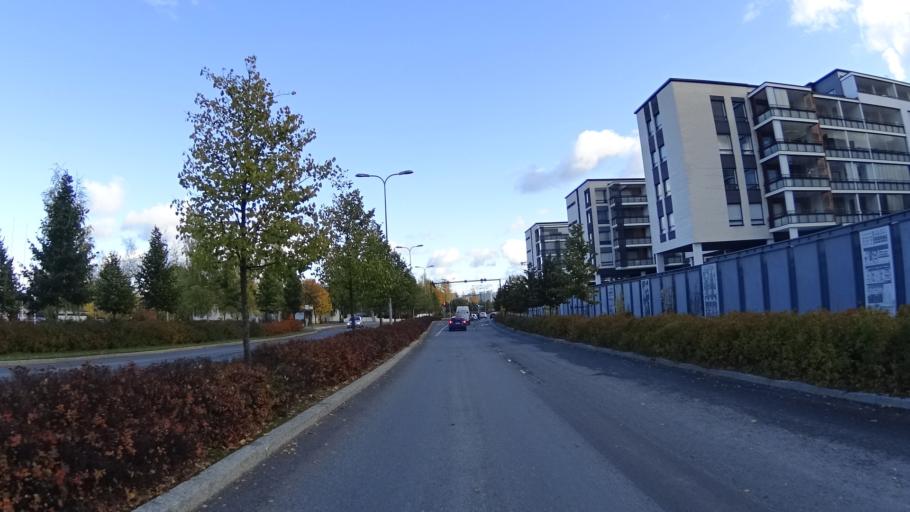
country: FI
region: Uusimaa
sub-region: Helsinki
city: Vantaa
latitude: 60.2913
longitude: 25.0198
